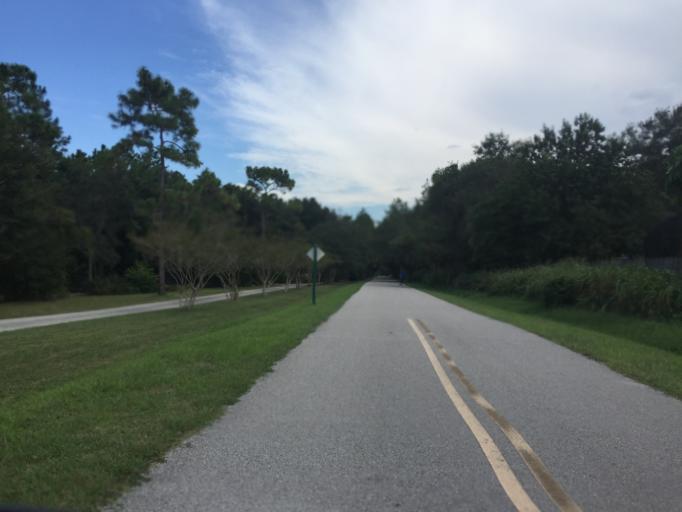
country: US
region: Florida
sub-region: Seminole County
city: Oviedo
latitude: 28.6792
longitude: -81.2207
